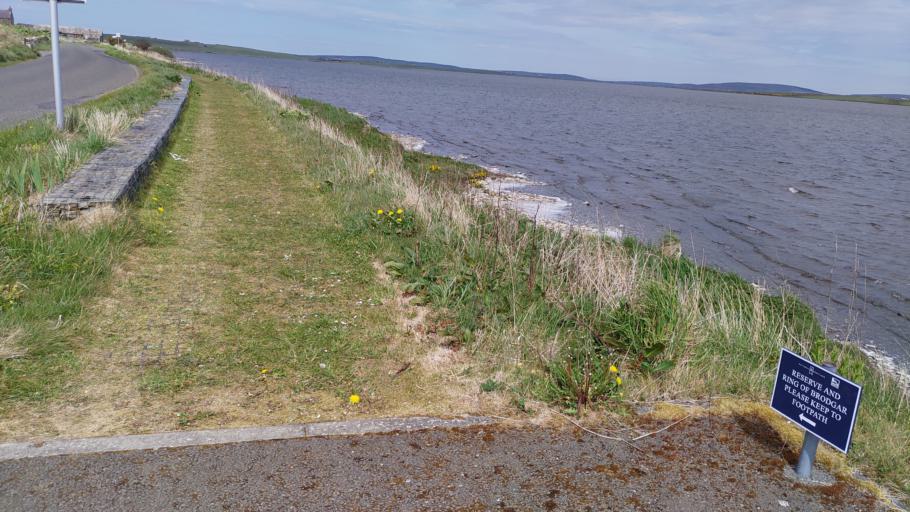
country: GB
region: Scotland
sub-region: Orkney Islands
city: Stromness
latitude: 58.9966
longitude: -3.2125
